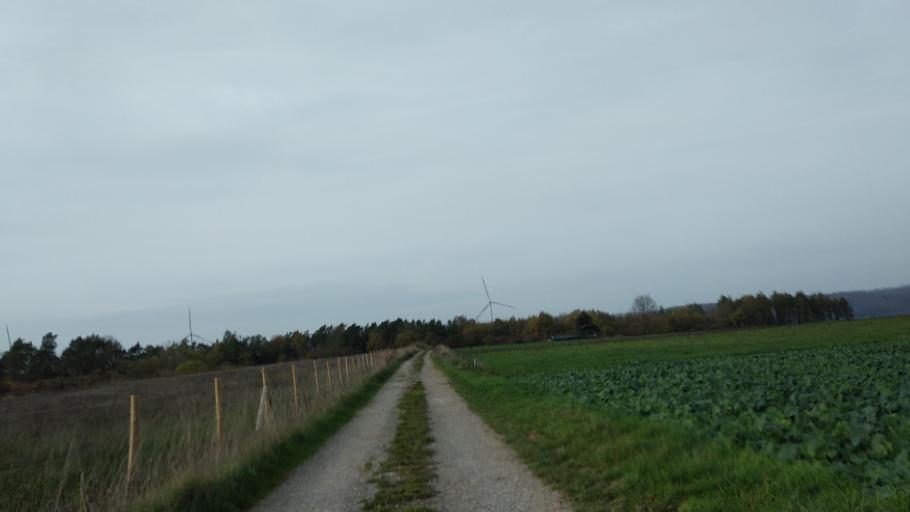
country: DE
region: North Rhine-Westphalia
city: Beverungen
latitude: 51.6907
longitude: 9.3394
